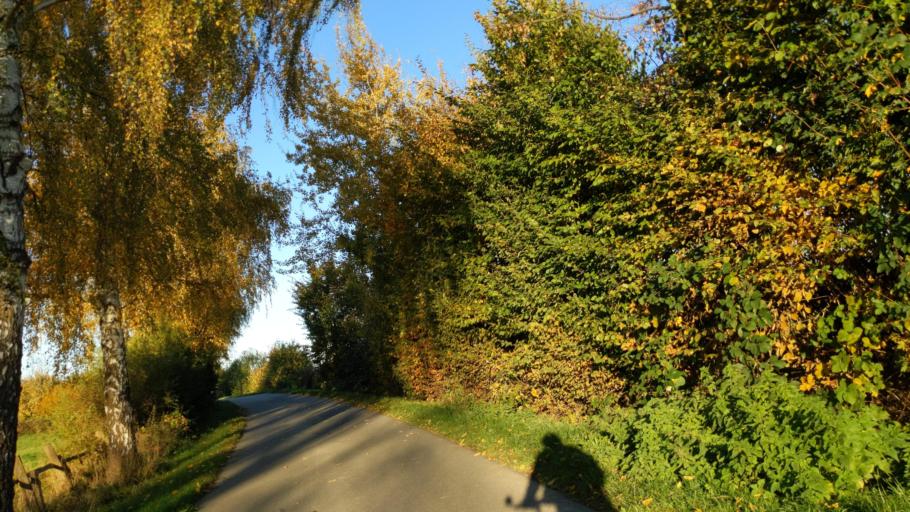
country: DE
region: Schleswig-Holstein
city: Pogeez
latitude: 53.7561
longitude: 10.7212
